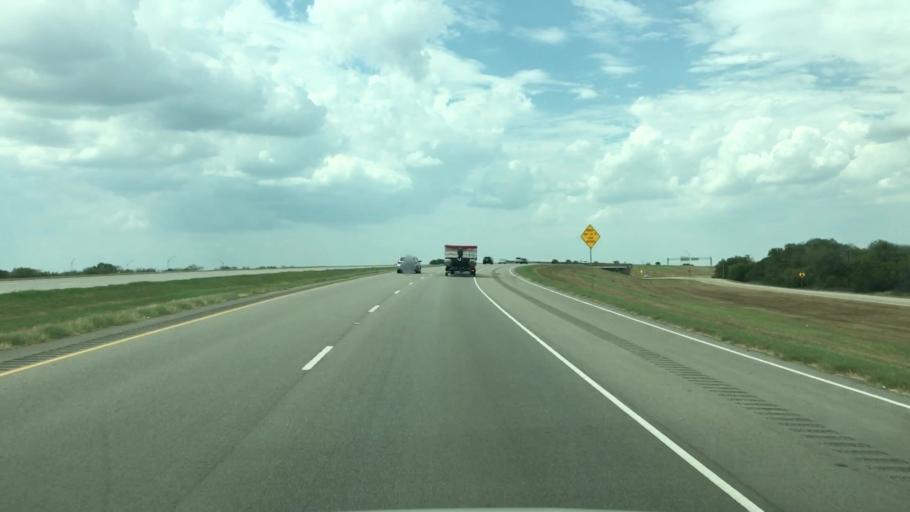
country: US
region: Texas
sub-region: Live Oak County
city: Three Rivers
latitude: 28.5230
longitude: -98.1836
